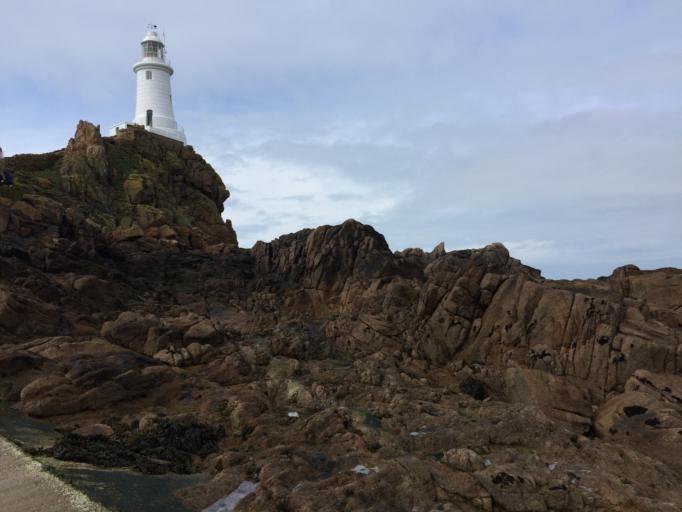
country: JE
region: St Helier
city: Saint Helier
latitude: 49.1799
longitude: -2.2488
